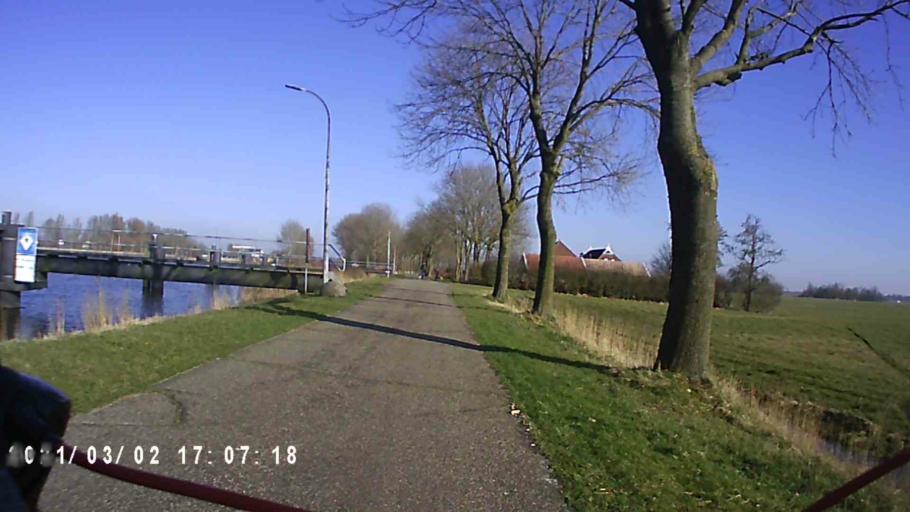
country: NL
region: Groningen
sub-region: Gemeente Zuidhorn
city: Grijpskerk
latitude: 53.2475
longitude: 6.3058
